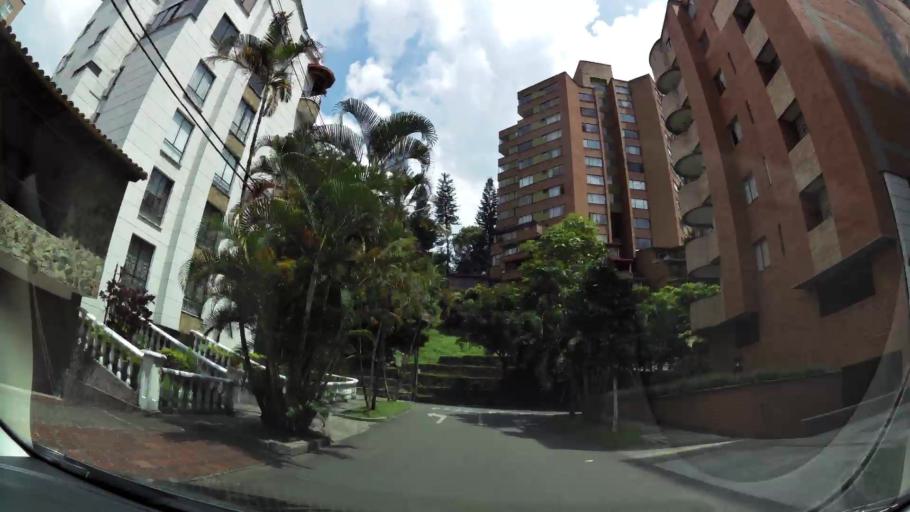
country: CO
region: Antioquia
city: Envigado
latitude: 6.1750
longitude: -75.5892
